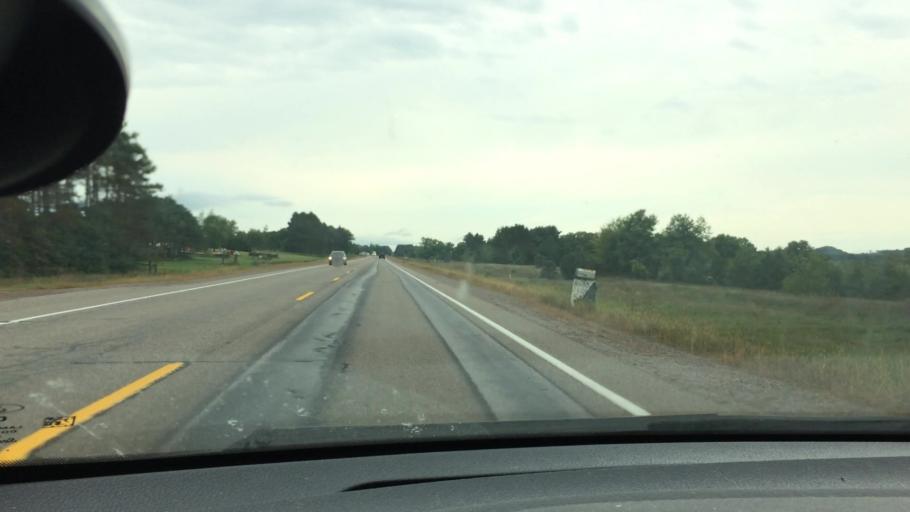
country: US
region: Wisconsin
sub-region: Eau Claire County
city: Augusta
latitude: 44.5841
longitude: -91.1005
